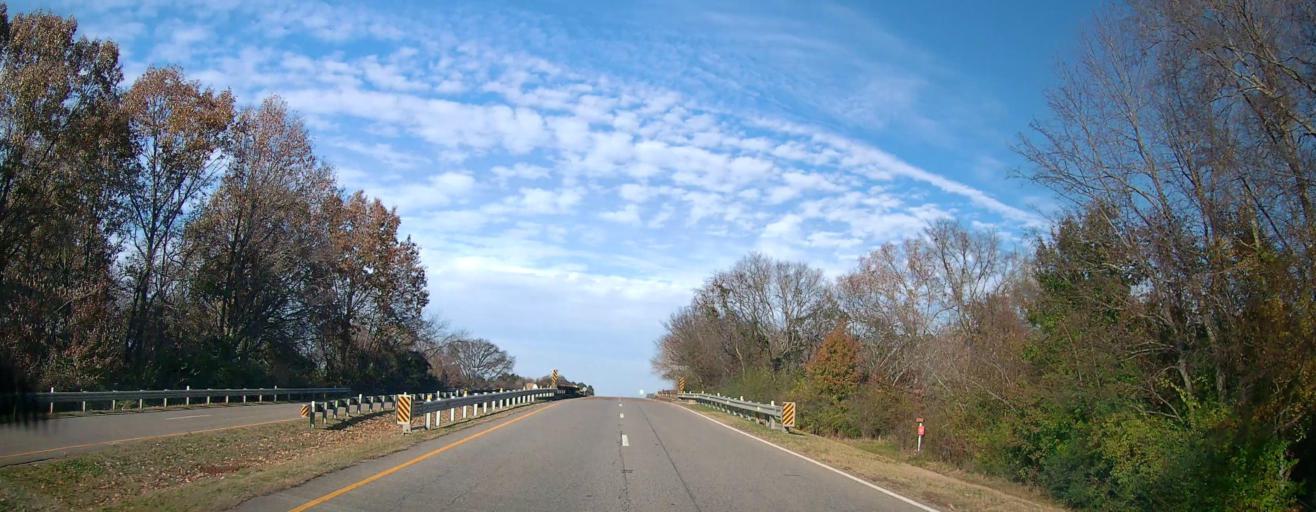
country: US
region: Alabama
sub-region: Morgan County
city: Decatur
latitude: 34.6320
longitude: -86.9508
